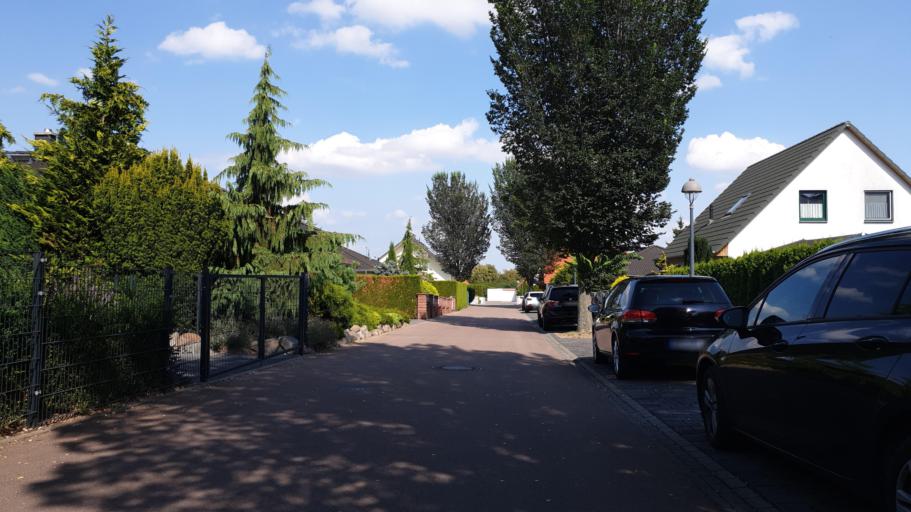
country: DE
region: Saxony-Anhalt
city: Bernburg
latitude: 51.7815
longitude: 11.7560
